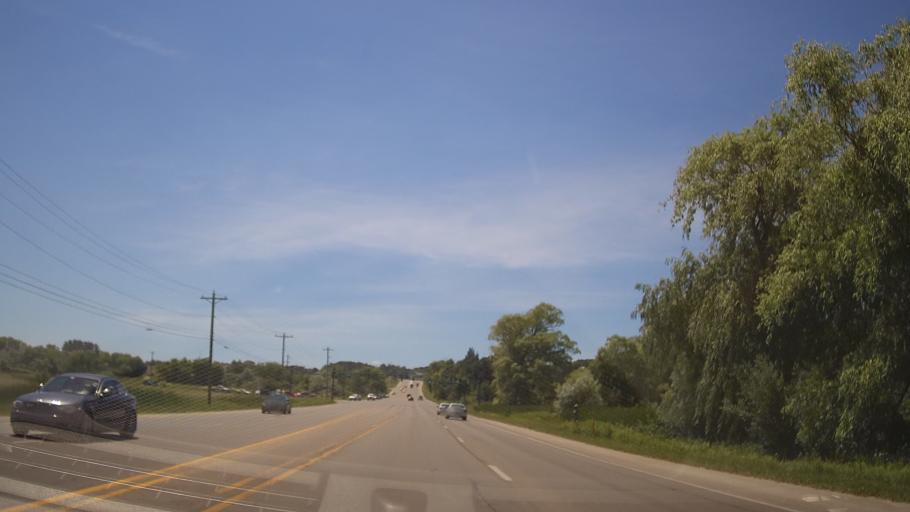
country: US
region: Michigan
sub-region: Grand Traverse County
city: Traverse City
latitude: 44.7484
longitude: -85.6432
